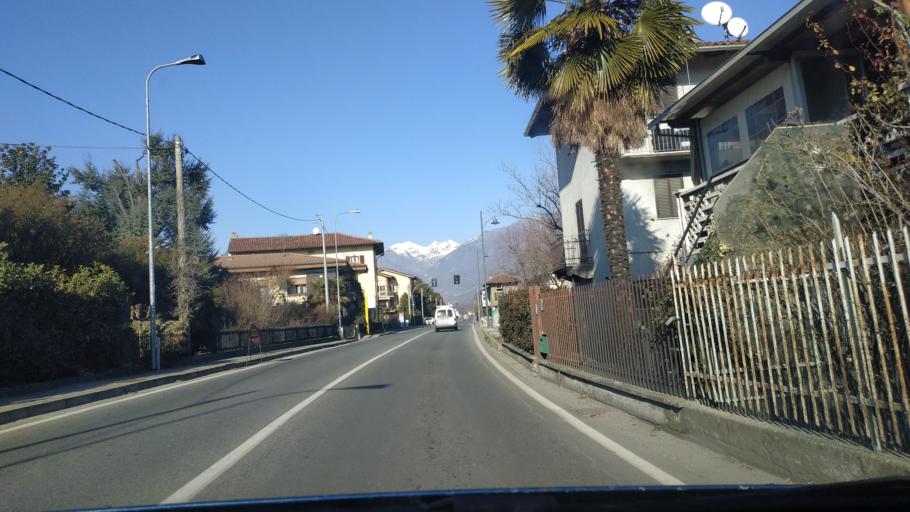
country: IT
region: Piedmont
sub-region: Provincia di Torino
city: Montalto Dora
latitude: 45.4935
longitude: 7.8598
